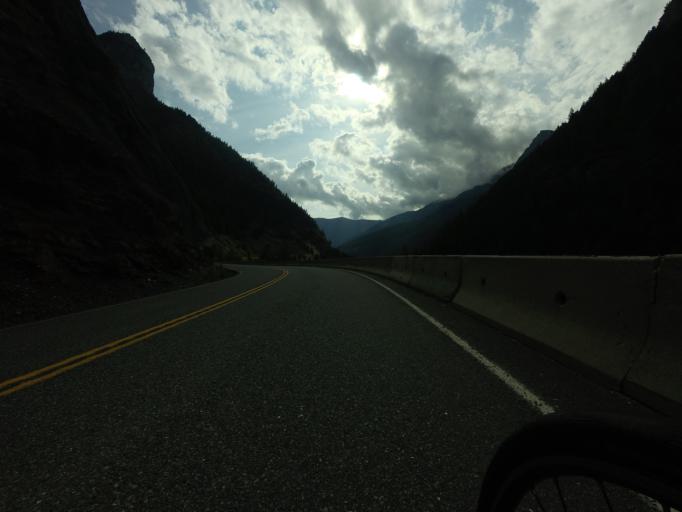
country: CA
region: British Columbia
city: Lillooet
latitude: 50.6415
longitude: -122.0517
